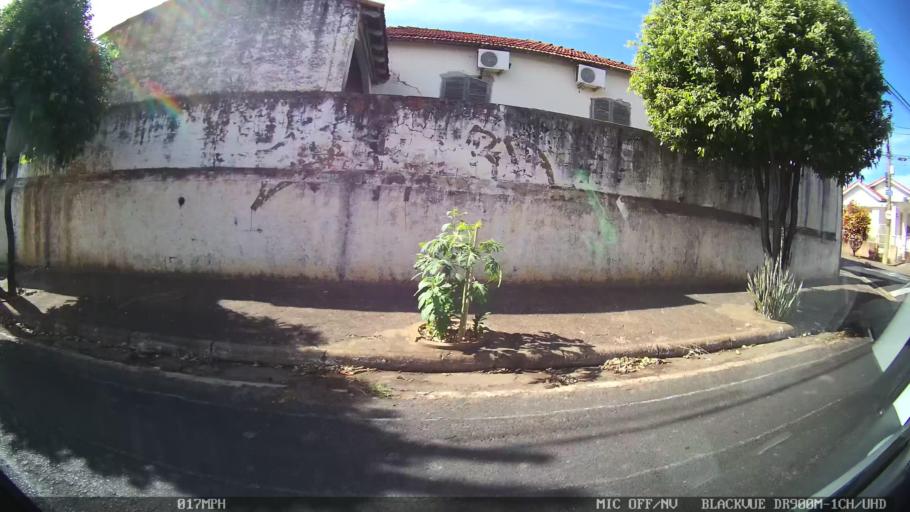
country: BR
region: Sao Paulo
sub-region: Catanduva
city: Catanduva
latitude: -21.1337
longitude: -48.9669
